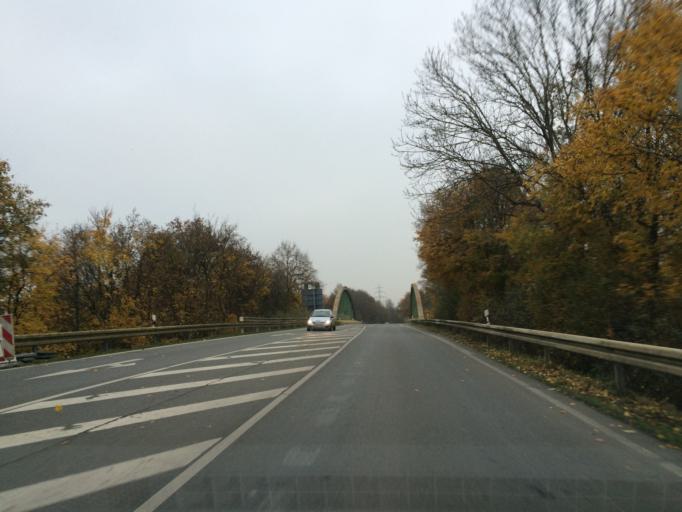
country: DE
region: North Rhine-Westphalia
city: Marl
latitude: 51.6849
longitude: 7.0712
